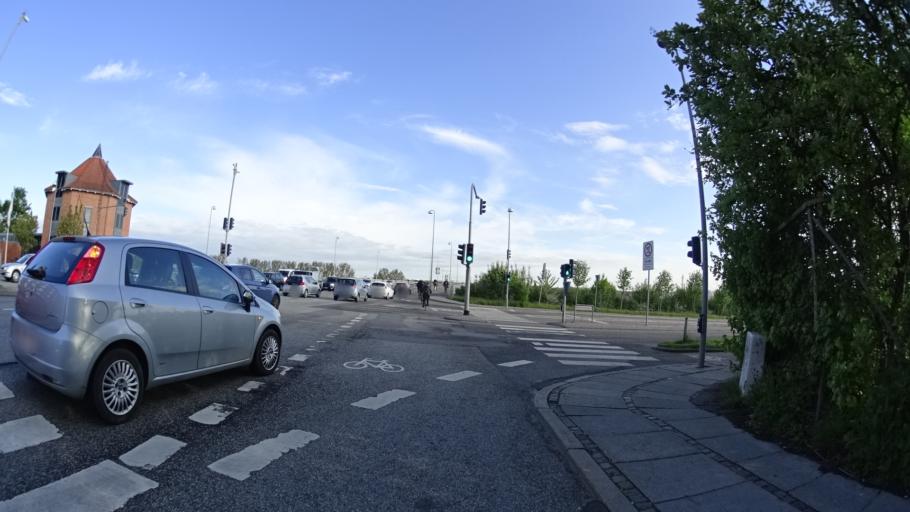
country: DK
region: Central Jutland
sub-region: Arhus Kommune
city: Arhus
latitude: 56.1469
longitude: 10.1859
